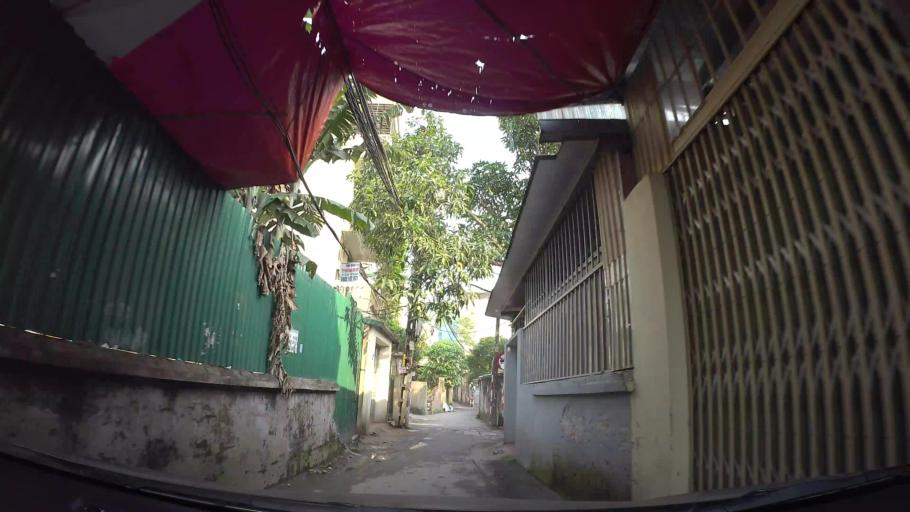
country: VN
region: Ha Noi
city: Thanh Xuan
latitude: 20.9785
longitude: 105.8293
